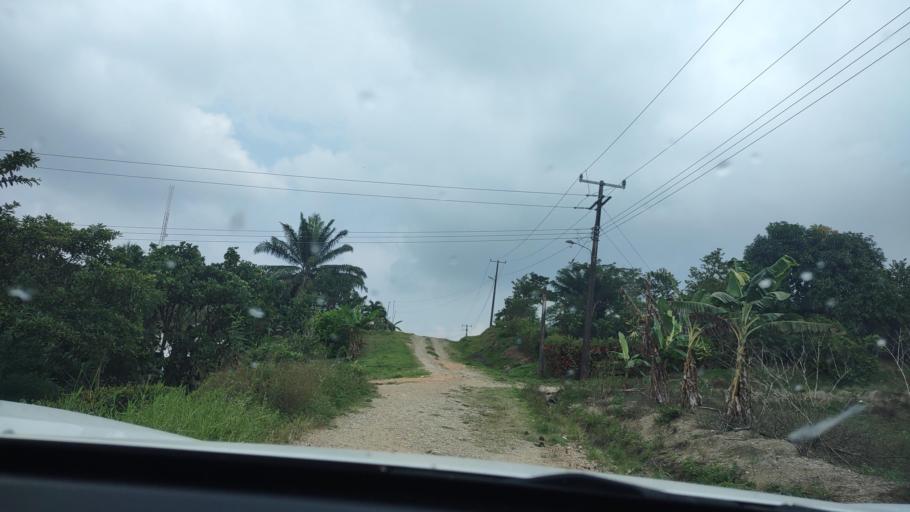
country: MX
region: Veracruz
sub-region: Uxpanapa
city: Poblado 10
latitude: 17.5479
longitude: -94.2934
